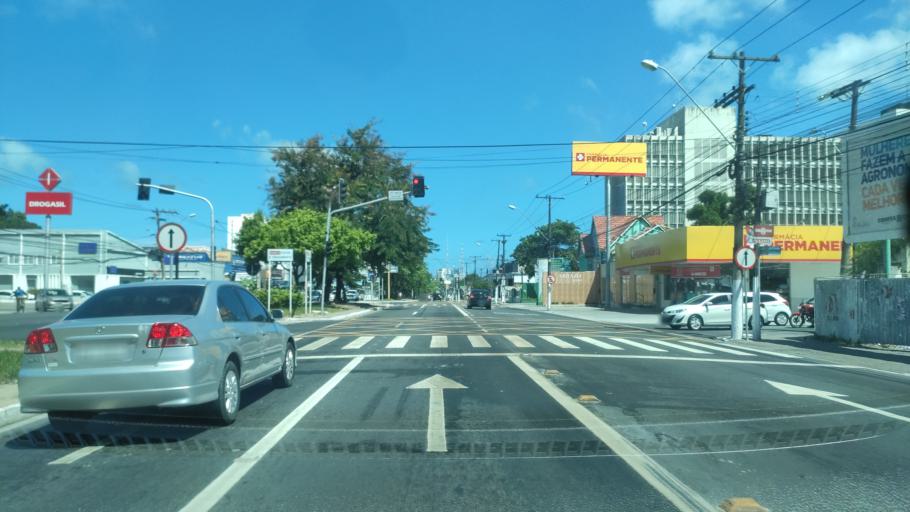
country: BR
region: Alagoas
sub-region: Maceio
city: Maceio
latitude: -9.6462
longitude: -35.7343
